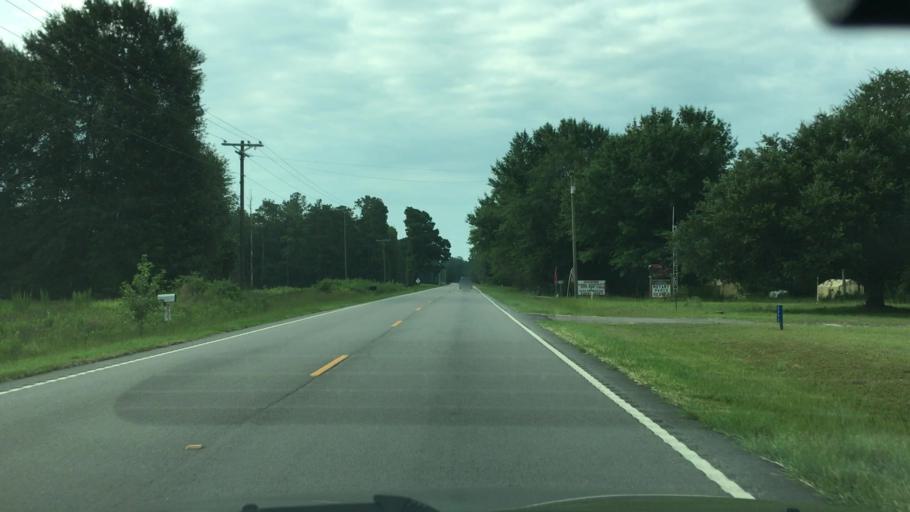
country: US
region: South Carolina
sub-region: Lexington County
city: Batesburg
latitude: 33.7175
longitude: -81.5003
